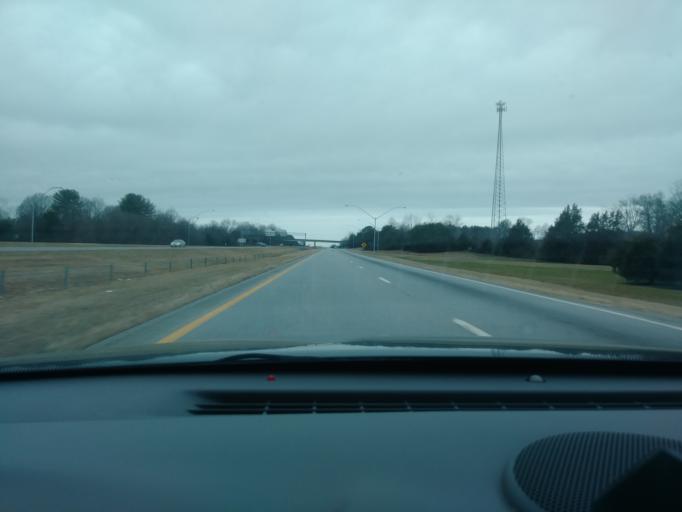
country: US
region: North Carolina
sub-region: Yadkin County
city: Jonesville
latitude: 36.1224
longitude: -80.8155
